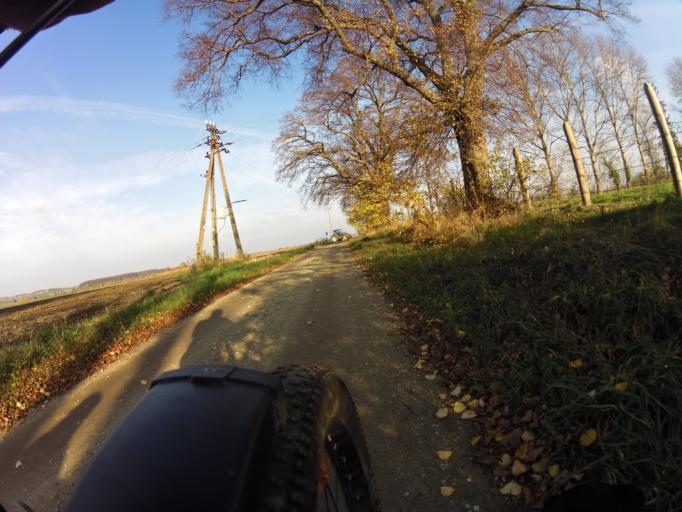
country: PL
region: Pomeranian Voivodeship
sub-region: Powiat pucki
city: Krokowa
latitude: 54.7656
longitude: 18.2438
